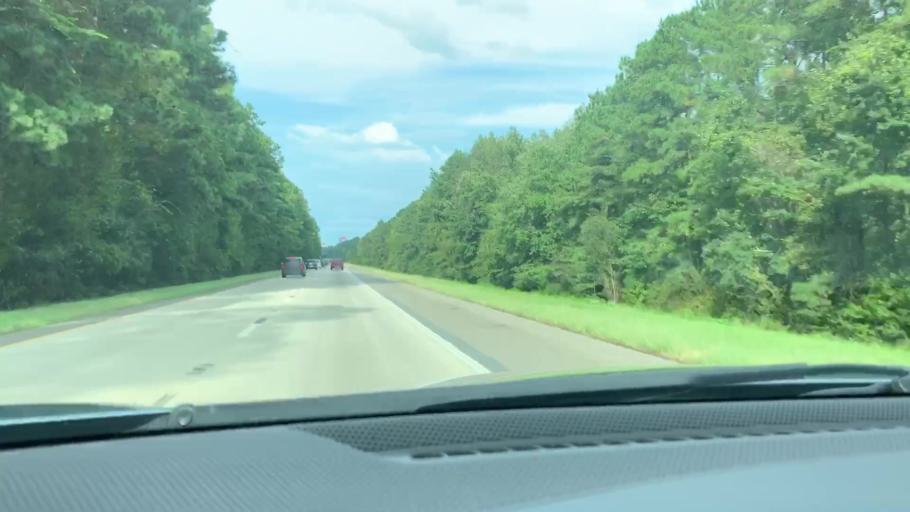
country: US
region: South Carolina
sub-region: Colleton County
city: Walterboro
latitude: 32.9015
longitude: -80.7051
